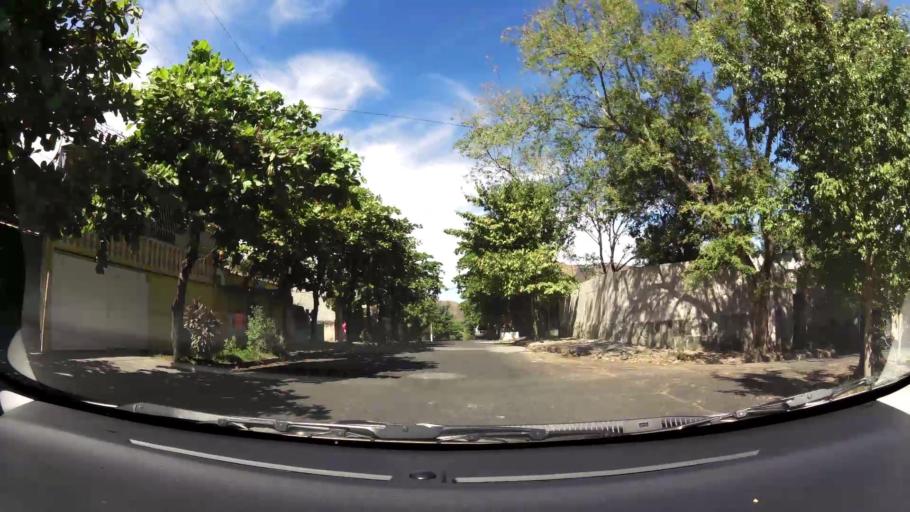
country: SV
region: San Salvador
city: Apopa
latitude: 13.8079
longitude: -89.1765
